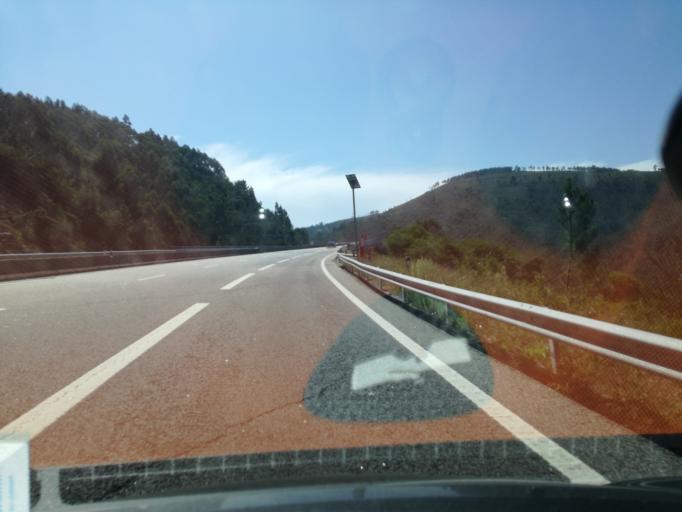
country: PT
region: Viana do Castelo
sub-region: Vila Nova de Cerveira
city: Vila Nova de Cerveira
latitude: 41.8657
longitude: -8.7806
